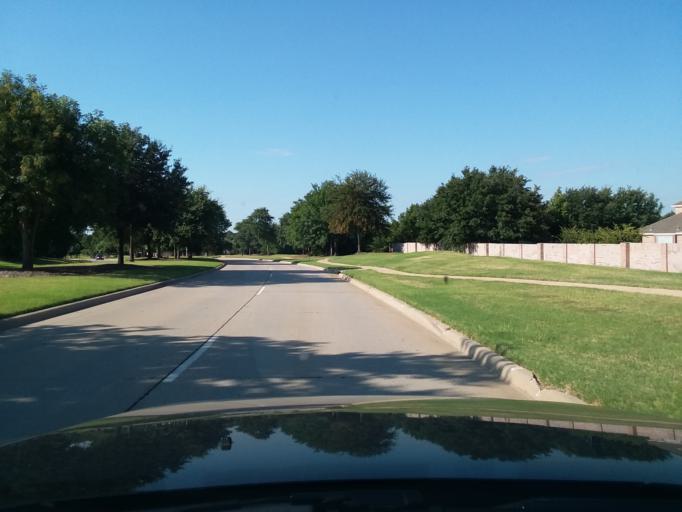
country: US
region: Texas
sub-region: Denton County
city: Double Oak
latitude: 33.0569
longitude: -97.0955
